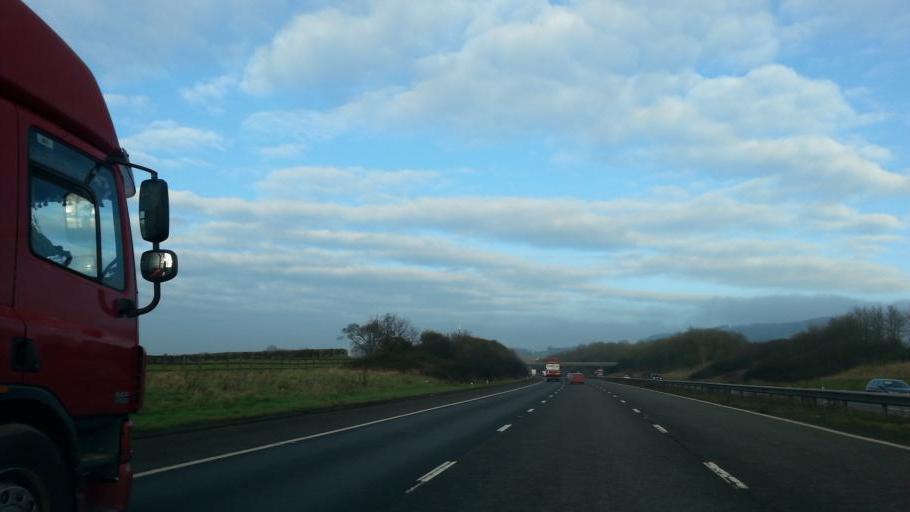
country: GB
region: England
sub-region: South Gloucestershire
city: Charfield
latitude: 51.6663
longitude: -2.4121
